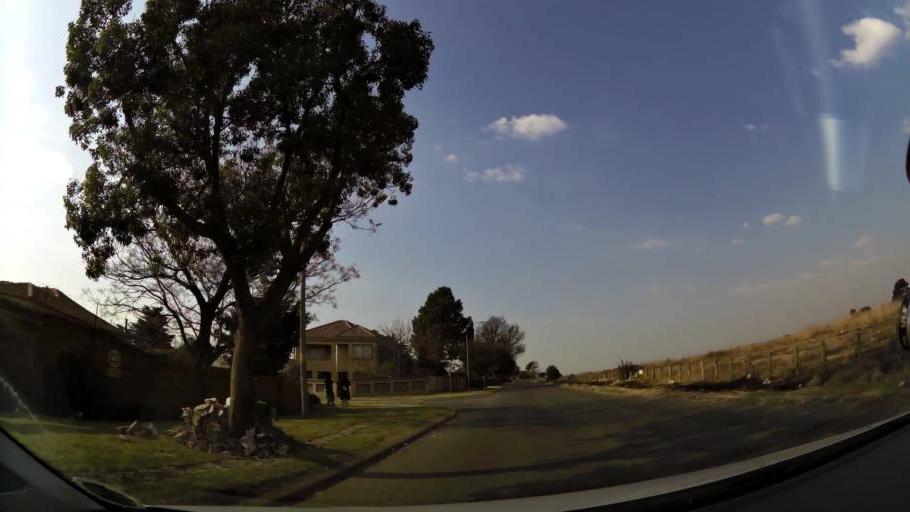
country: ZA
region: Gauteng
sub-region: City of Johannesburg Metropolitan Municipality
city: Modderfontein
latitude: -26.1050
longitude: 28.1913
